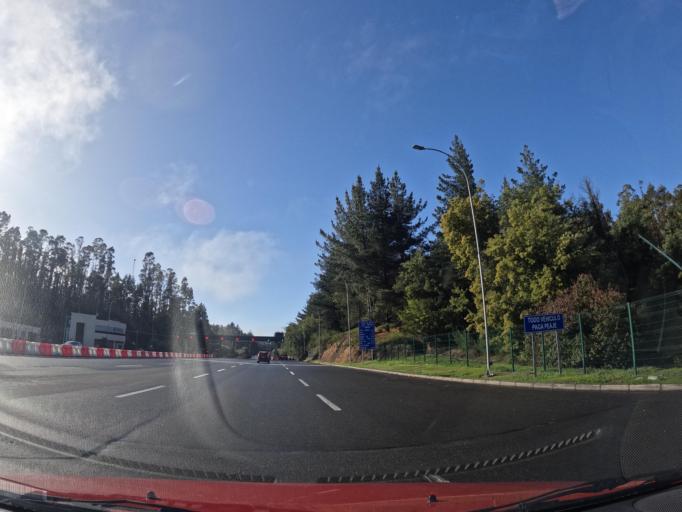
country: CL
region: Biobio
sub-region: Provincia de Concepcion
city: Penco
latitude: -36.7302
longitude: -72.8614
